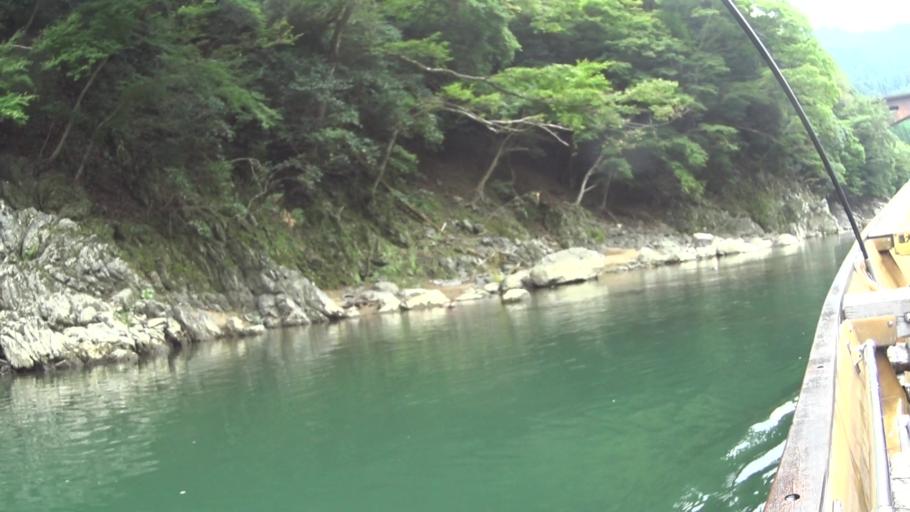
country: JP
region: Kyoto
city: Kameoka
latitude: 35.0210
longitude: 135.6260
